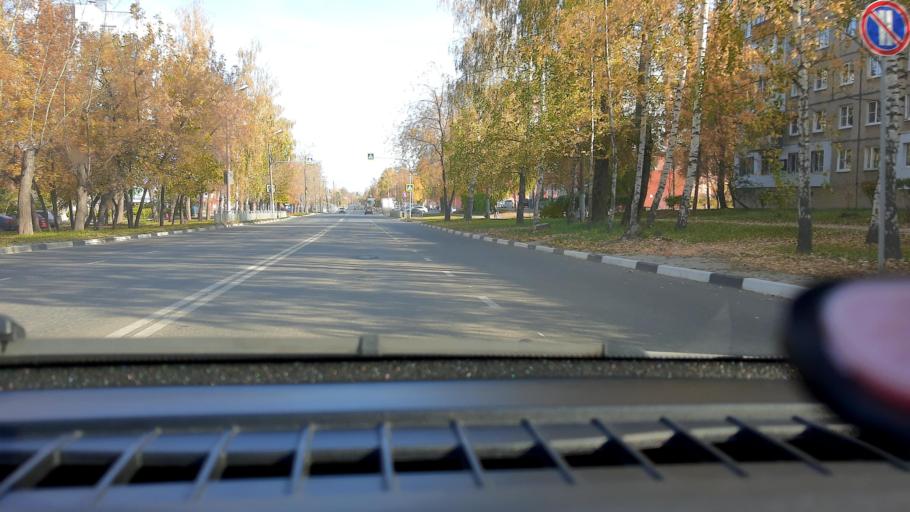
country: RU
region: Nizjnij Novgorod
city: Kstovo
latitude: 56.1495
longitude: 44.1844
